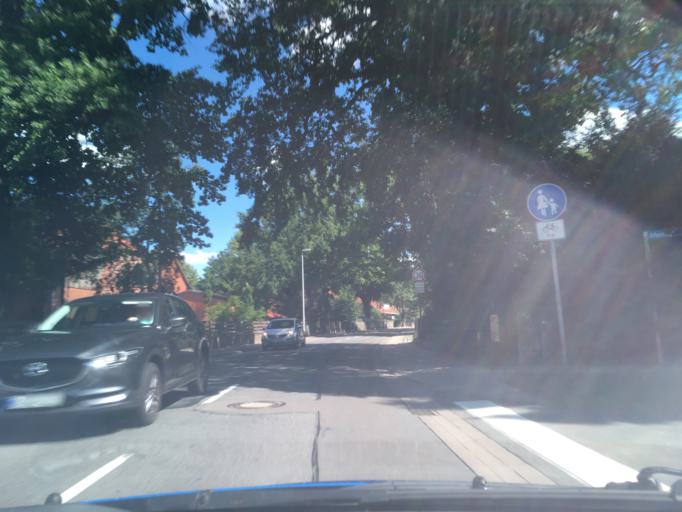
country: DE
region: Lower Saxony
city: Celle
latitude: 52.6355
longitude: 10.1100
